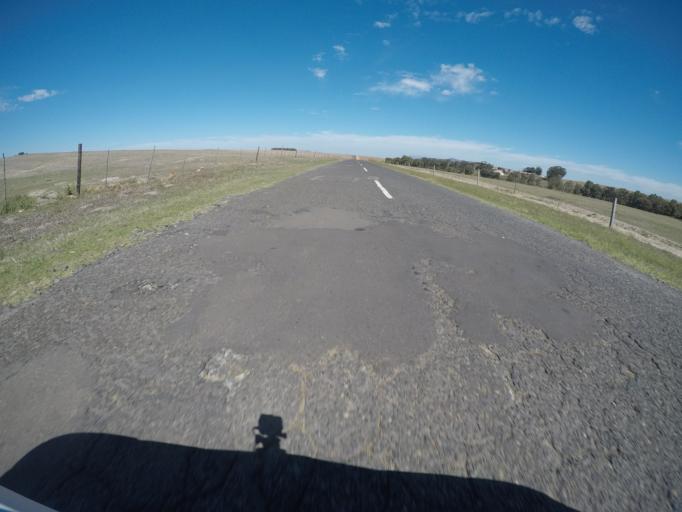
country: ZA
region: Western Cape
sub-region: City of Cape Town
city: Atlantis
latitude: -33.6243
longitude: 18.6308
